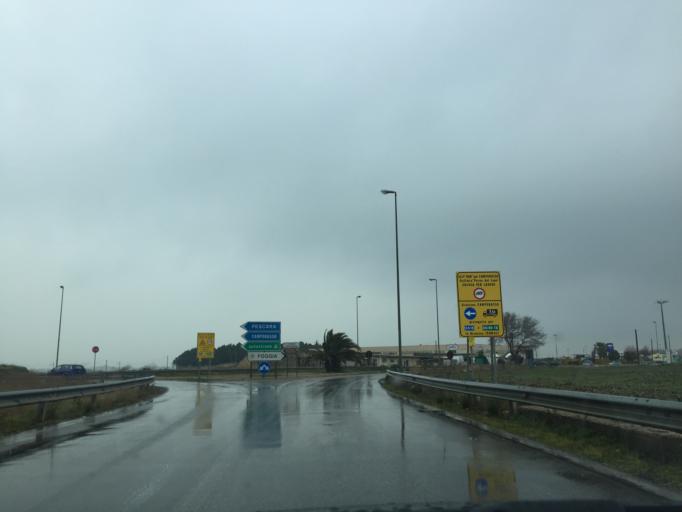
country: IT
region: Apulia
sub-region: Provincia di Foggia
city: Foggia
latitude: 41.4711
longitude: 15.5082
